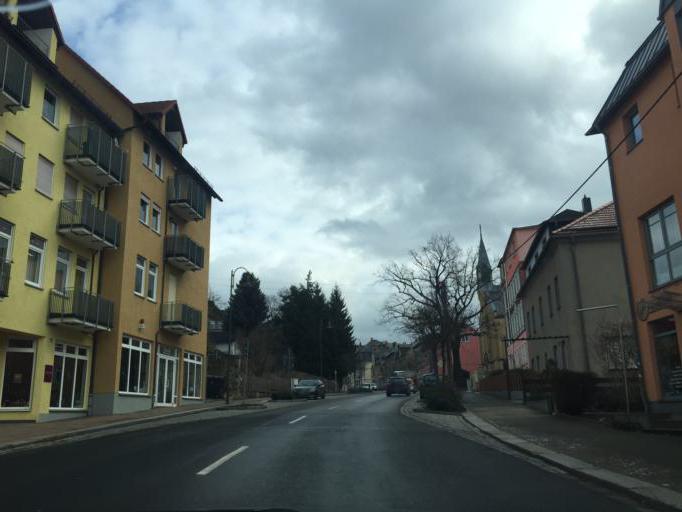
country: DE
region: Saxony
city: Radeberg
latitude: 51.1145
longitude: 13.9102
